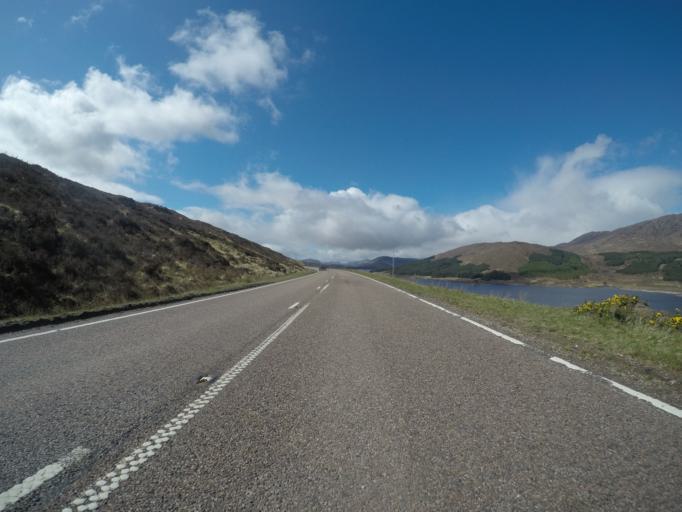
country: GB
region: Scotland
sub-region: Highland
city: Spean Bridge
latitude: 57.1199
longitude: -4.9770
